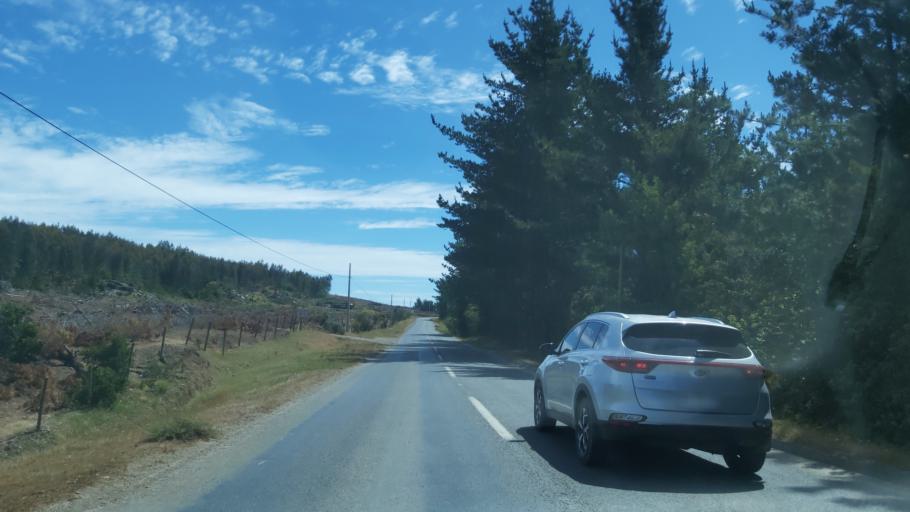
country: CL
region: Maule
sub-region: Provincia de Talca
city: Constitucion
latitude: -35.5382
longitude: -72.5493
